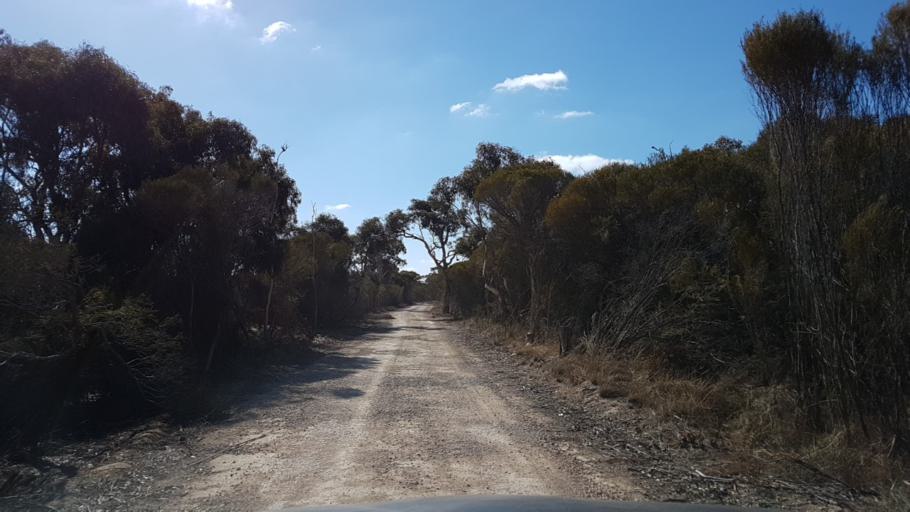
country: AU
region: South Australia
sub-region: Alexandrina
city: Goolwa
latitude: -35.3784
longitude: 138.8312
